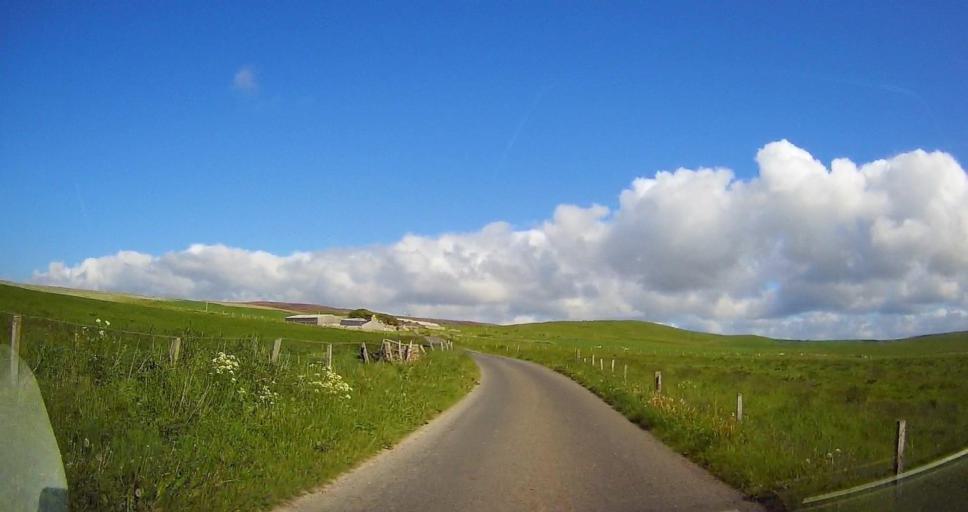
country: GB
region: Scotland
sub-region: Orkney Islands
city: Stromness
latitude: 58.9836
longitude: -3.1462
